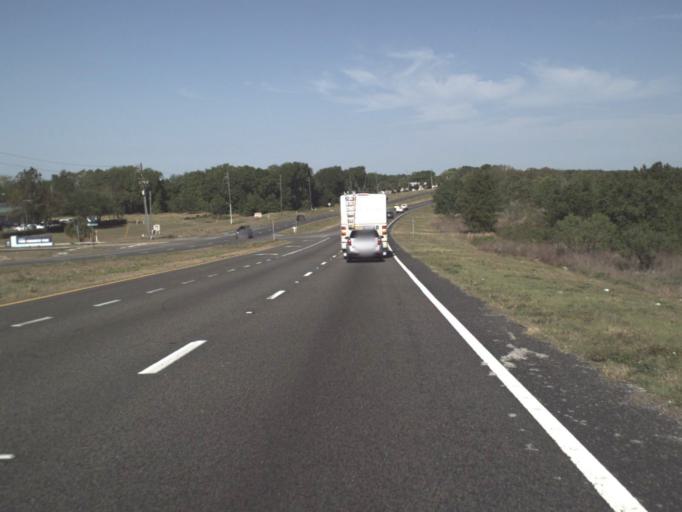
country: US
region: Florida
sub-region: Lake County
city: Howie In The Hills
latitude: 28.6469
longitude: -81.8265
